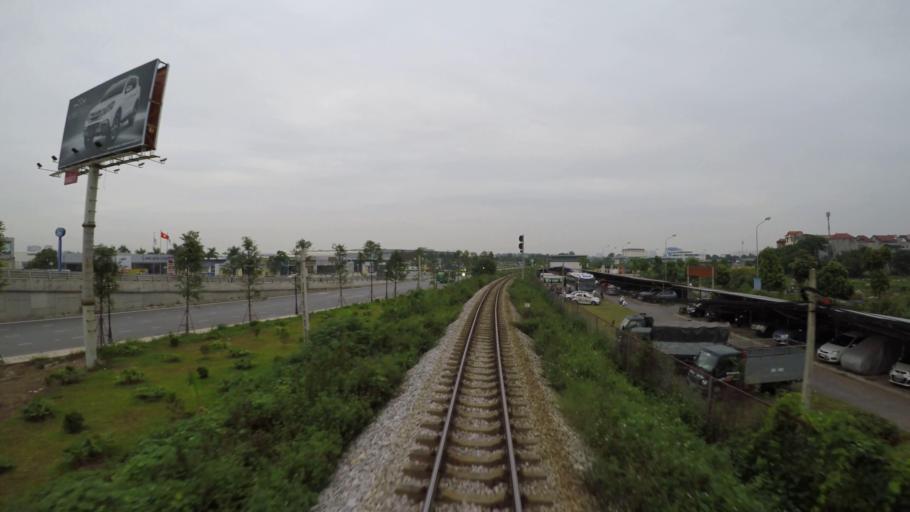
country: VN
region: Ha Noi
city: Trau Quy
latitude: 21.0170
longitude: 105.9439
